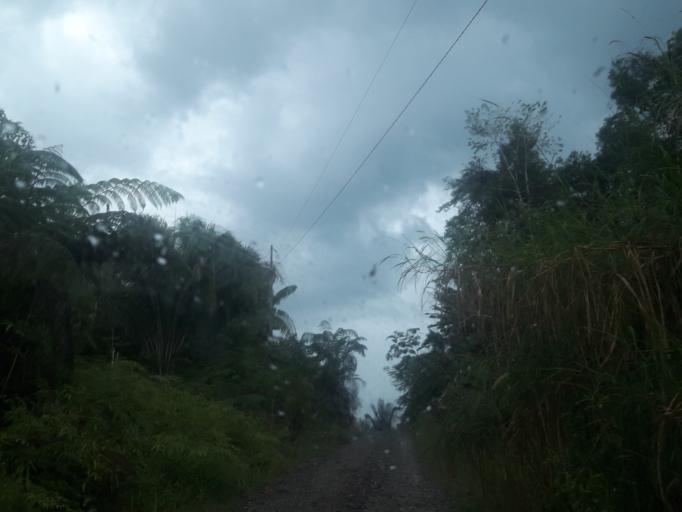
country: EC
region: Napo
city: Tena
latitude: -1.0902
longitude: -77.7055
